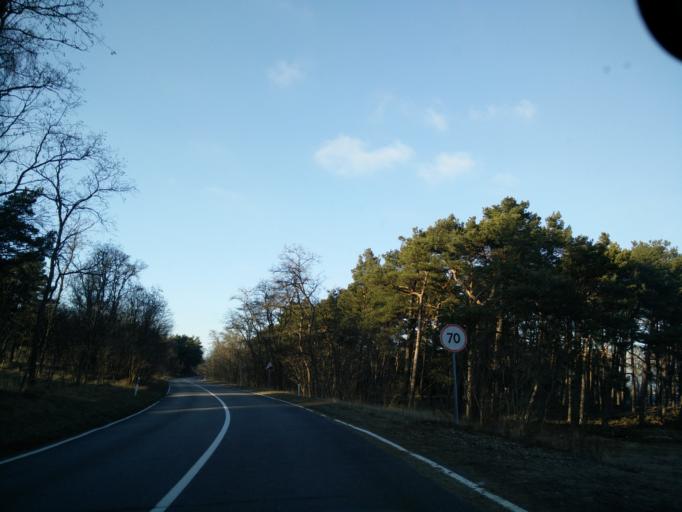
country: LT
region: Klaipedos apskritis
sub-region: Klaipeda
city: Klaipeda
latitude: 55.6362
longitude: 21.1302
